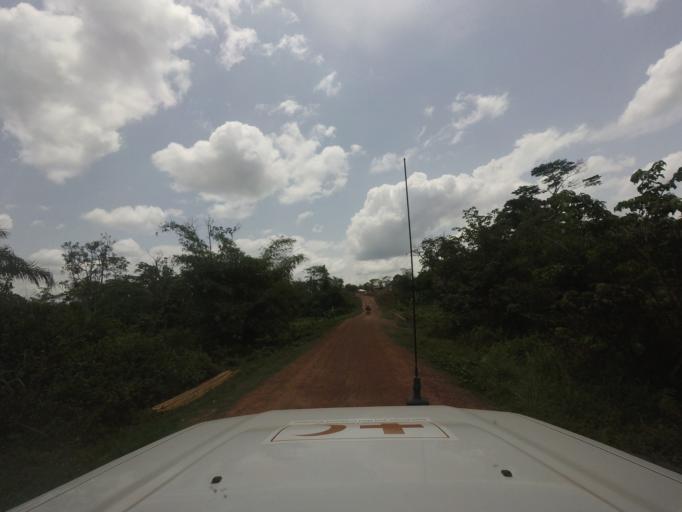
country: LR
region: Bong
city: Gbarnga
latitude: 7.1609
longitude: -9.2117
